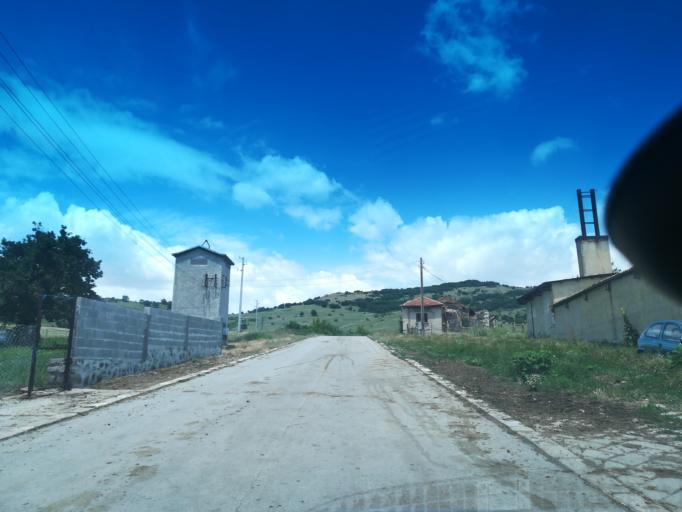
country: BG
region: Khaskovo
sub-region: Obshtina Mineralni Bani
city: Mineralni Bani
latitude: 41.9491
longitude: 25.2473
